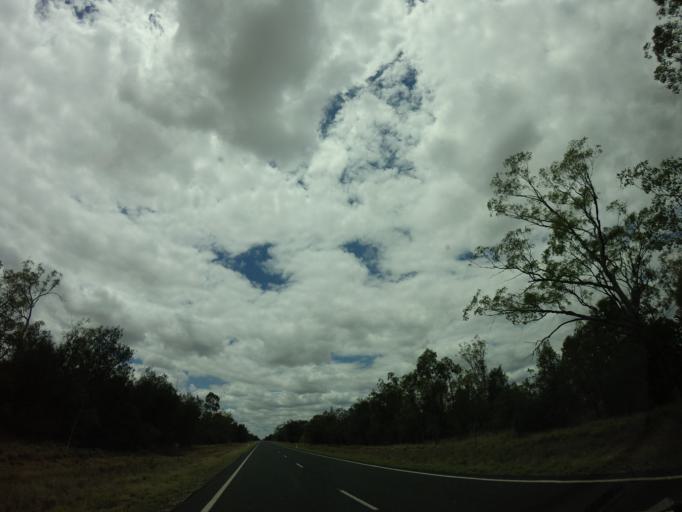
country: AU
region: Queensland
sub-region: Goondiwindi
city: Goondiwindi
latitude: -28.1719
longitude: 150.5757
